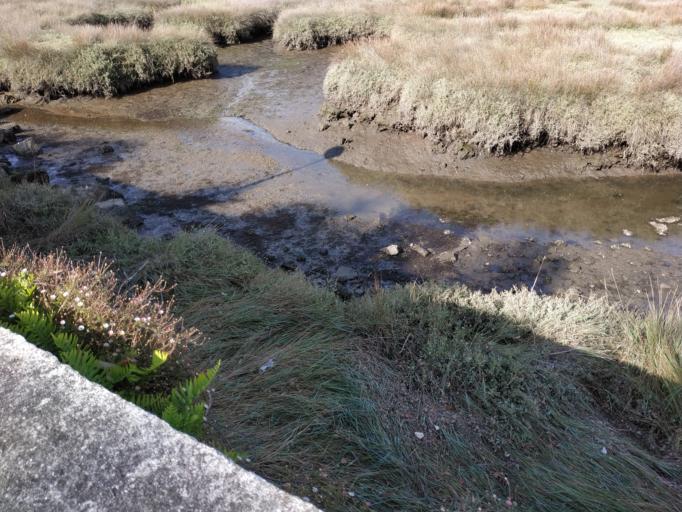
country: ES
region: Galicia
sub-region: Provincia da Coruna
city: Culleredo
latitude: 43.3217
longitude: -8.3733
